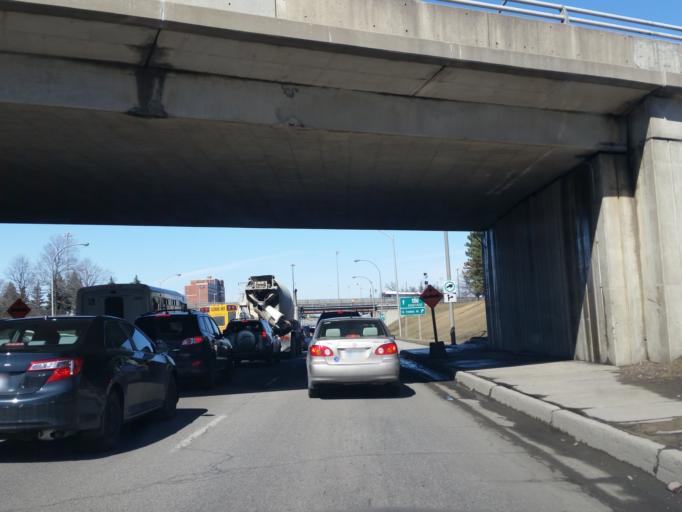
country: CA
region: Ontario
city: Ottawa
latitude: 45.4141
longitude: -75.6573
